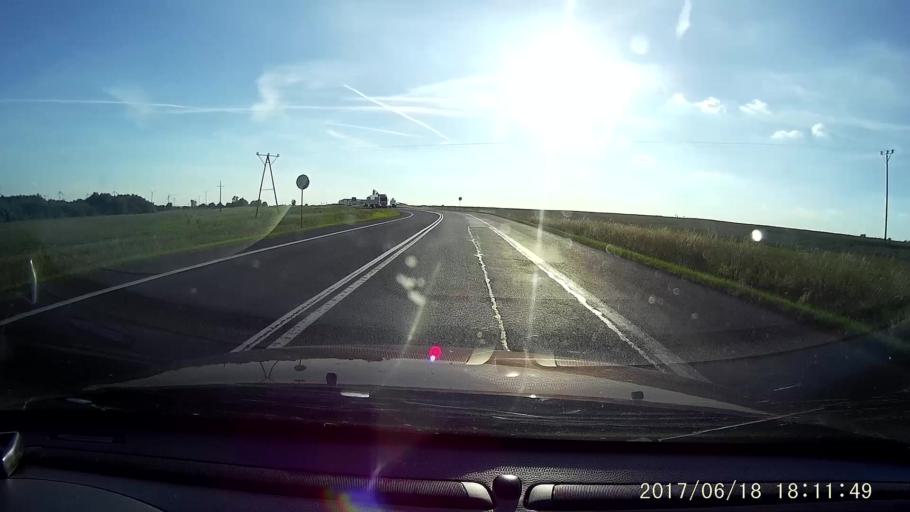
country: PL
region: Lower Silesian Voivodeship
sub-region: Powiat zgorzelecki
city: Piensk
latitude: 51.2048
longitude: 15.1174
